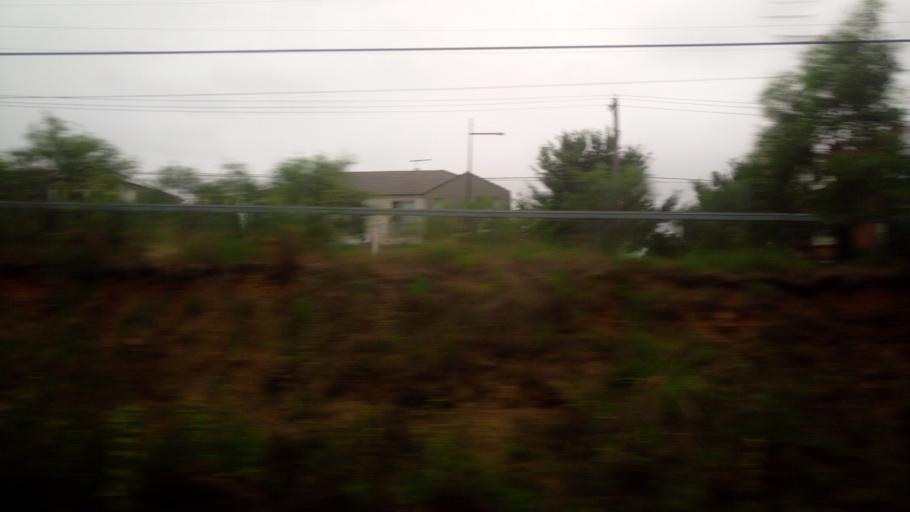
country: AU
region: New South Wales
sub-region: Blacktown
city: Doonside
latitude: -33.7634
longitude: 150.8773
